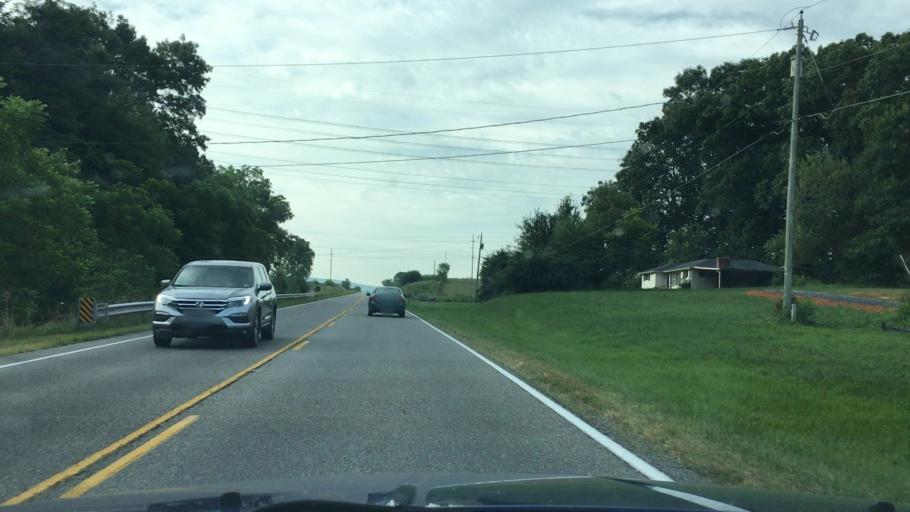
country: US
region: Virginia
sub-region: Augusta County
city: Dooms
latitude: 38.1233
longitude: -78.9139
